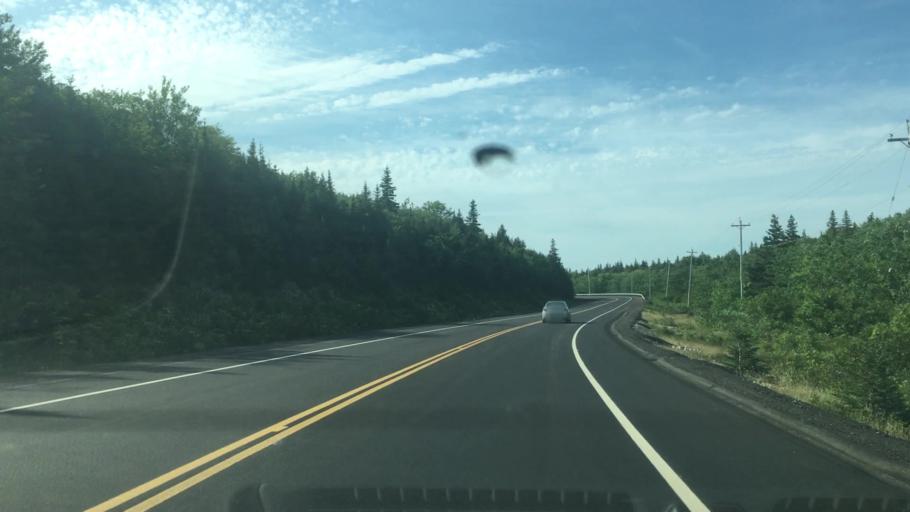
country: CA
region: Nova Scotia
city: Sydney Mines
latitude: 46.8381
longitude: -60.3854
